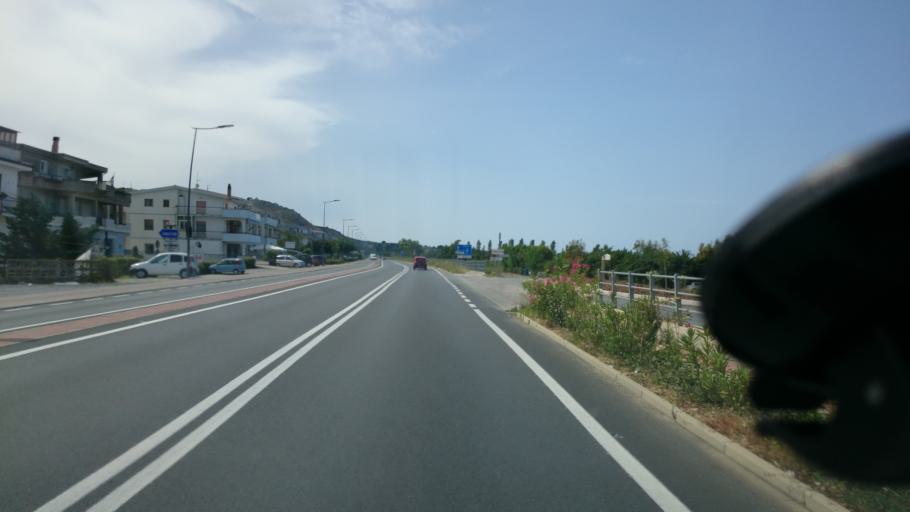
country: IT
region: Calabria
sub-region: Provincia di Cosenza
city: Santa Maria del Cedro
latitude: 39.7361
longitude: 15.8090
